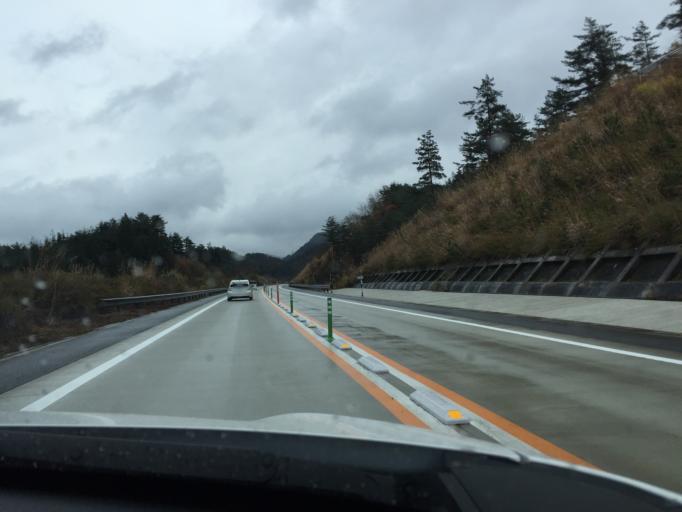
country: JP
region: Yamagata
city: Yonezawa
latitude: 37.8805
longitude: 140.1815
